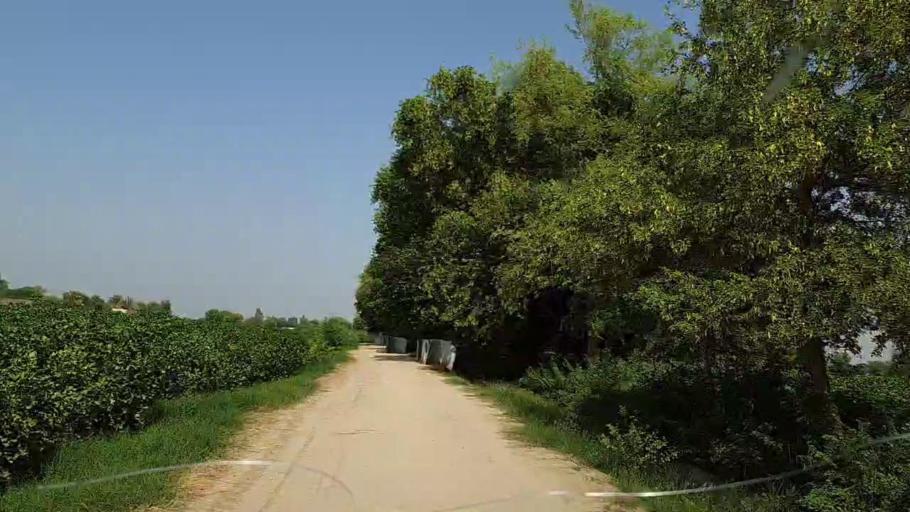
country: PK
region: Sindh
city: Khanpur
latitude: 27.7544
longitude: 69.3607
